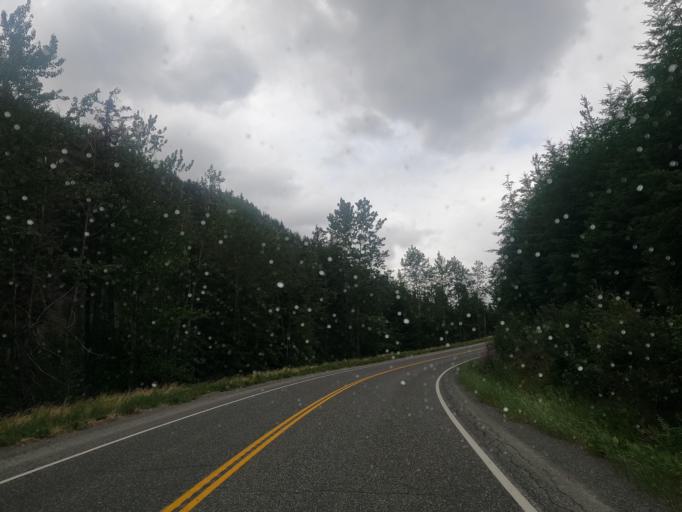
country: CA
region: British Columbia
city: Lillooet
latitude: 50.4927
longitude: -122.1956
